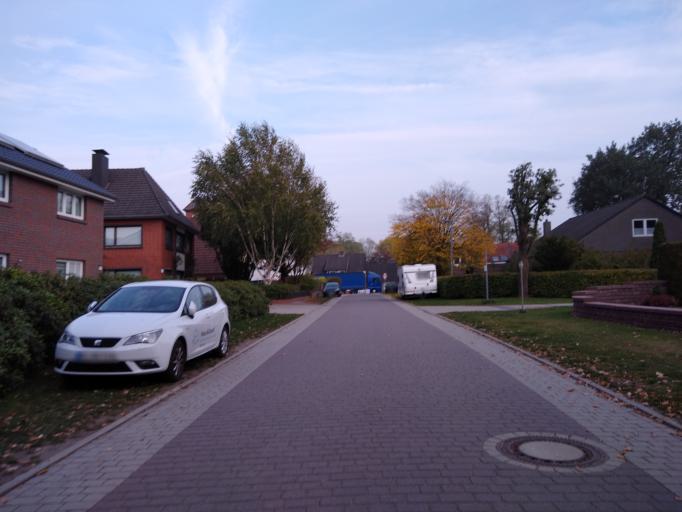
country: DE
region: Lower Saxony
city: Rastede
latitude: 53.2107
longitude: 8.2467
